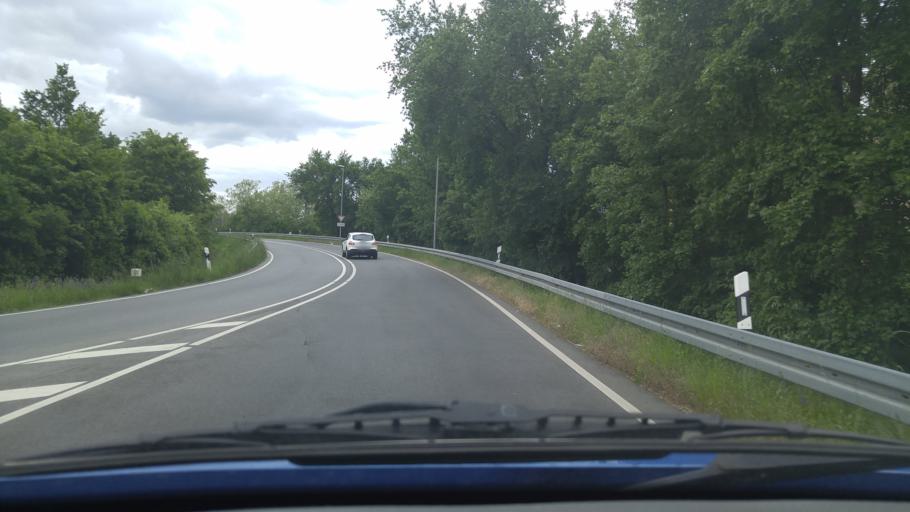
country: DE
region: Hesse
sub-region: Regierungsbezirk Darmstadt
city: Florsheim
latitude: 50.0027
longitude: 8.4263
